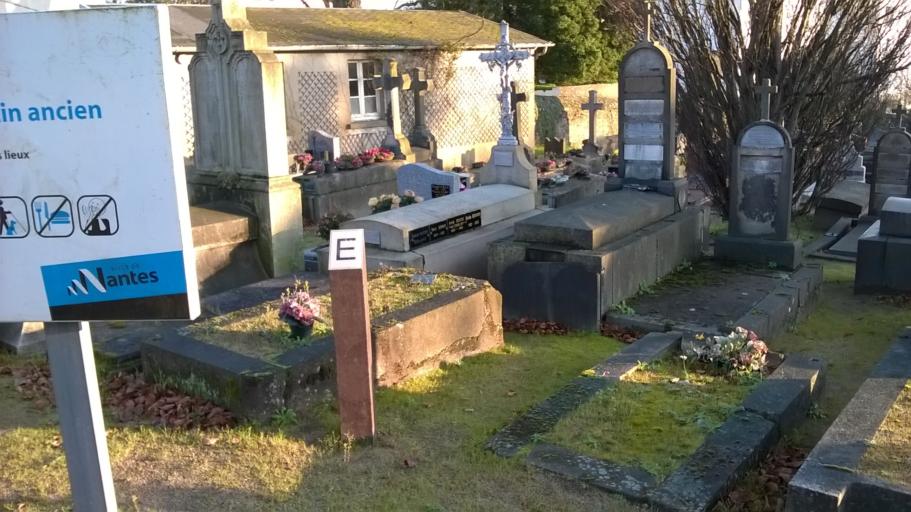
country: FR
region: Pays de la Loire
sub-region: Departement de la Loire-Atlantique
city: Bouguenais
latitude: 47.1992
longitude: -1.5921
